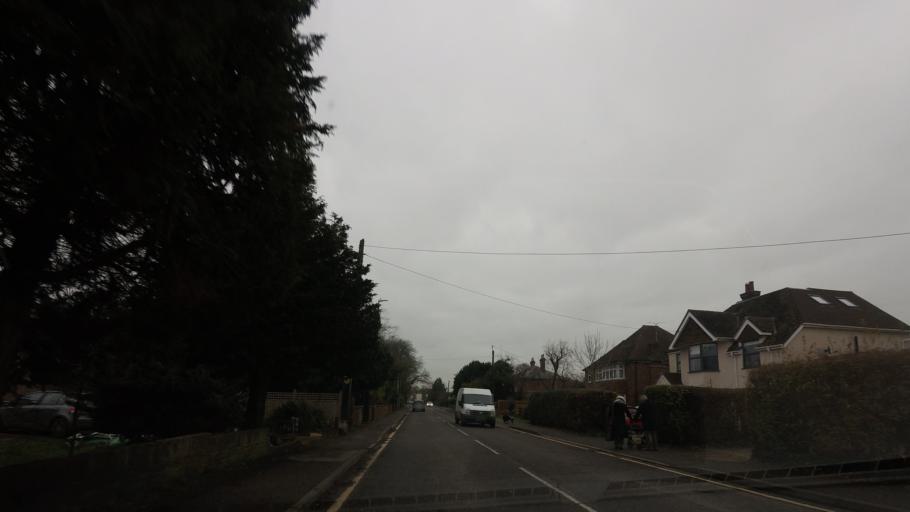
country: GB
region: England
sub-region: Kent
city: Staplehurst
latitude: 51.1676
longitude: 0.5526
